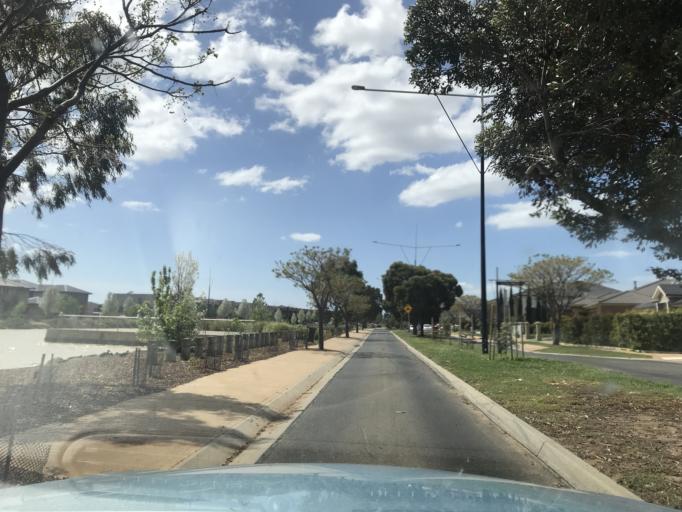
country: AU
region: Victoria
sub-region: Wyndham
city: Williams Landing
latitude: -37.8575
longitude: 144.7344
